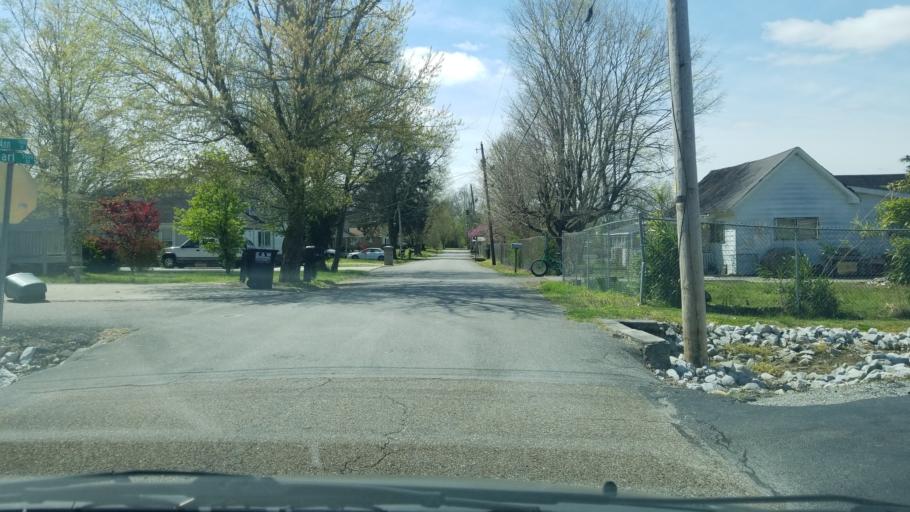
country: US
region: Tennessee
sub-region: Hamilton County
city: Collegedale
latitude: 35.0717
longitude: -85.0619
